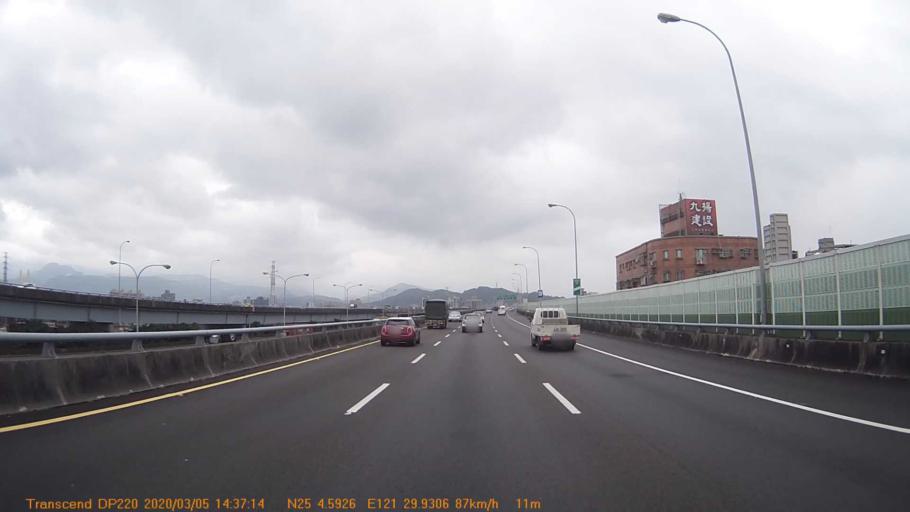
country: TW
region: Taipei
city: Taipei
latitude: 25.0758
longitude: 121.4991
